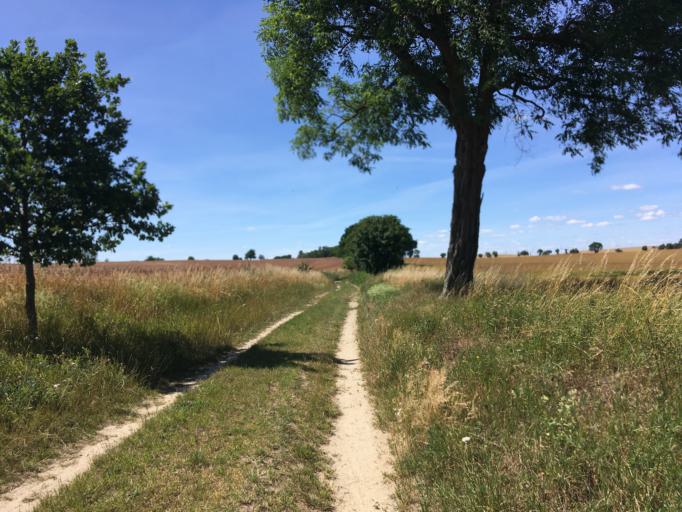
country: DE
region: Brandenburg
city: Brussow
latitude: 53.3269
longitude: 14.0799
